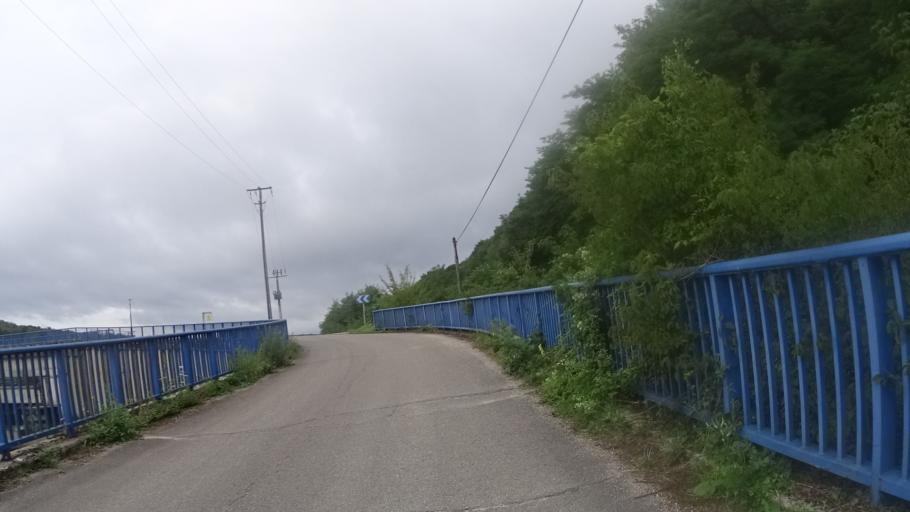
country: FR
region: Lorraine
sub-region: Departement de Meurthe-et-Moselle
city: Gondreville
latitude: 48.6522
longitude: 5.9784
